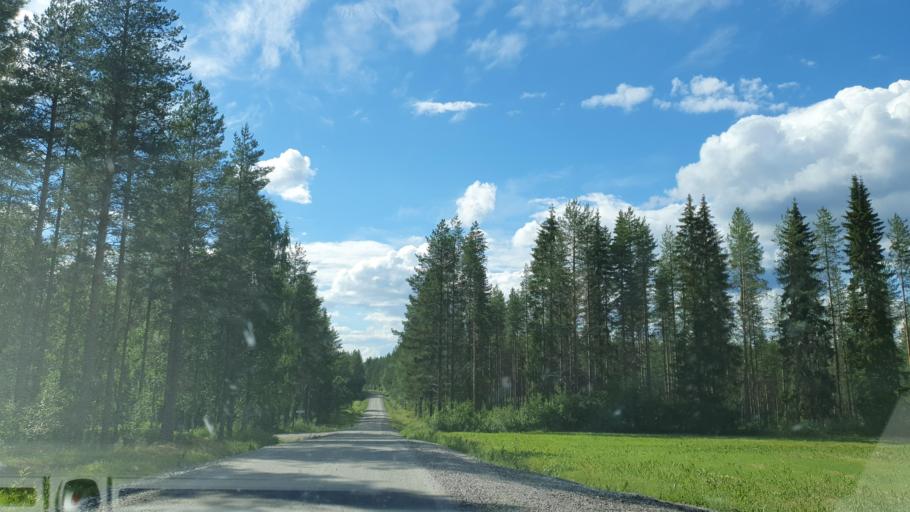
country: FI
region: Kainuu
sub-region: Kehys-Kainuu
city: Kuhmo
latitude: 64.1461
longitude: 29.7706
